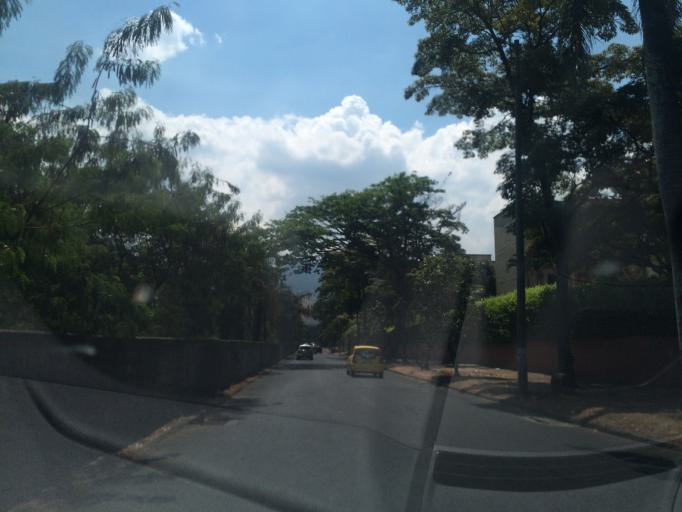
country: CO
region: Valle del Cauca
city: Cali
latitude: 3.4819
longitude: -76.5104
